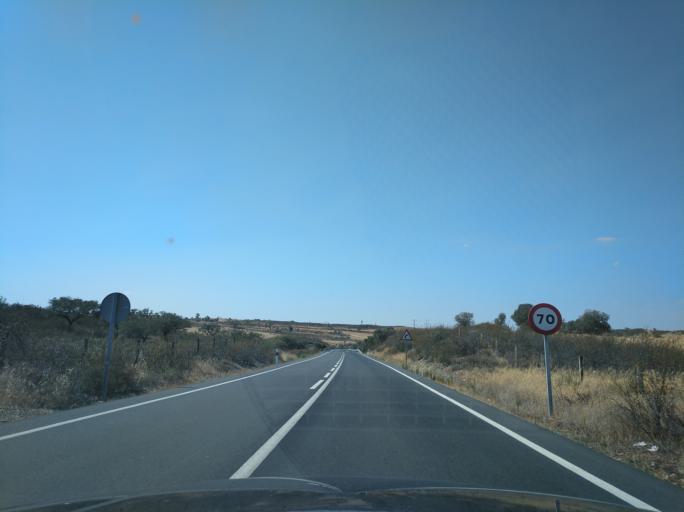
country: ES
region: Andalusia
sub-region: Provincia de Huelva
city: San Bartolome de la Torre
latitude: 37.4699
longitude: -7.1246
